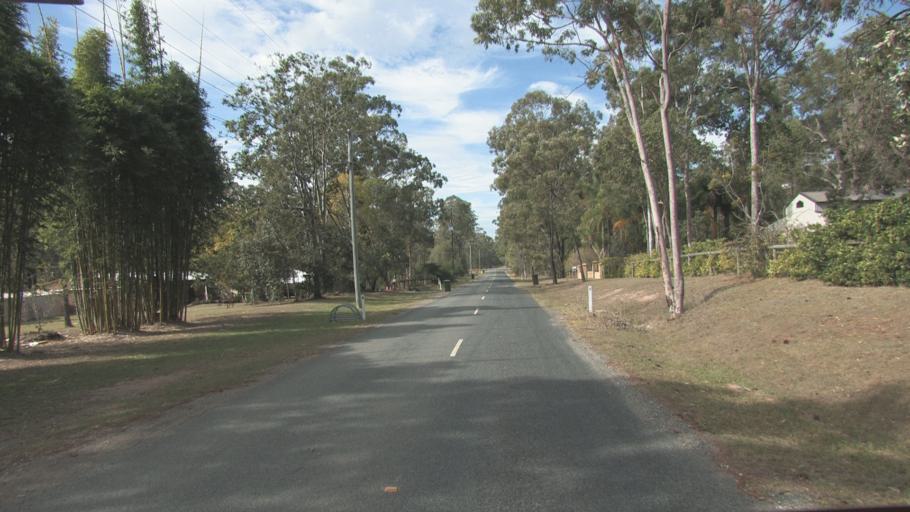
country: AU
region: Queensland
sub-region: Logan
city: North Maclean
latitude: -27.7605
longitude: 152.9838
